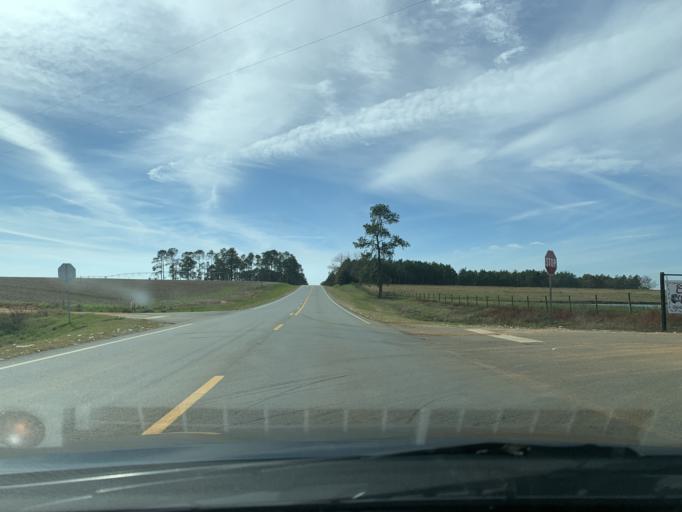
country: US
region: Georgia
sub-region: Turner County
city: Ashburn
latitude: 31.7837
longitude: -83.5114
